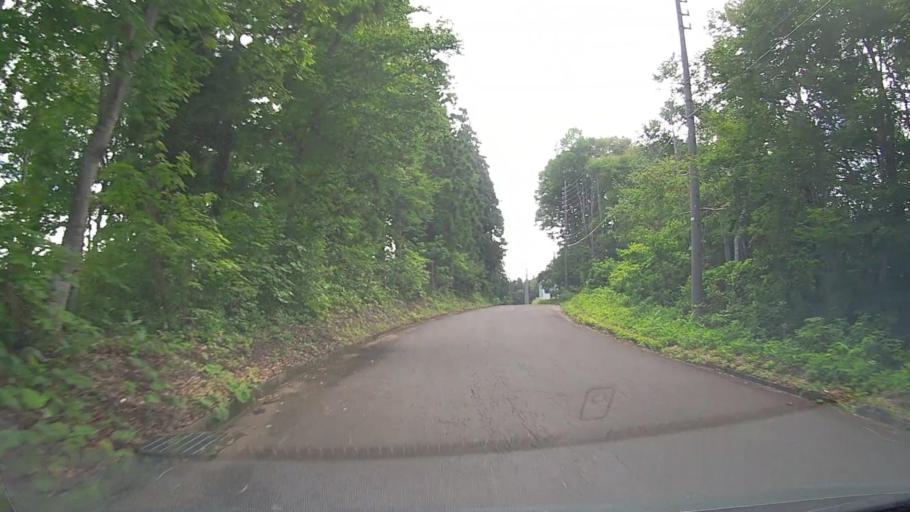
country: JP
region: Nagano
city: Iiyama
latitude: 36.9194
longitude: 138.4812
